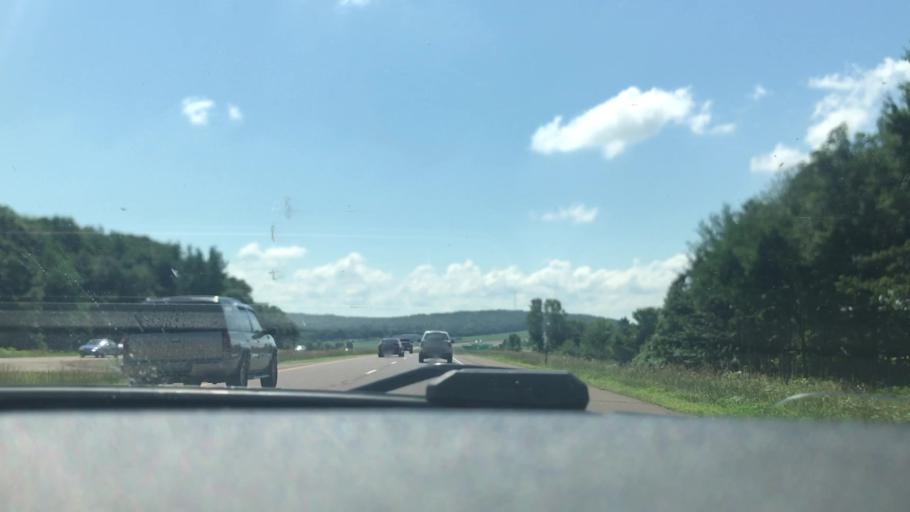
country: US
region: Wisconsin
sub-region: Chippewa County
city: Chippewa Falls
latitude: 44.9740
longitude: -91.4337
